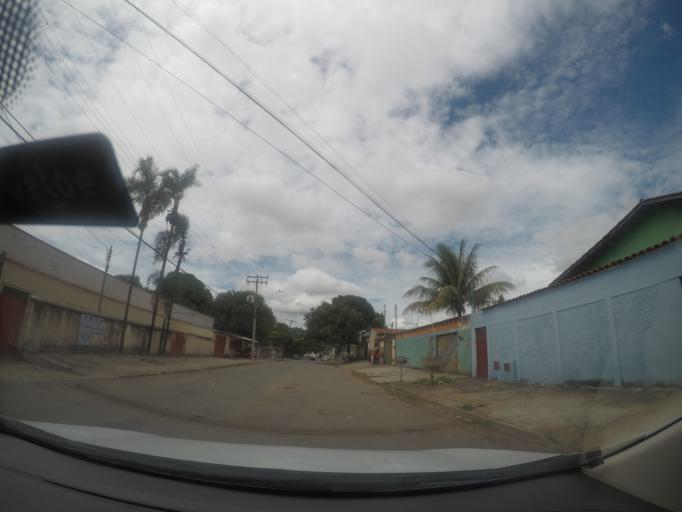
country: BR
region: Goias
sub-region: Goiania
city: Goiania
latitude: -16.6597
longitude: -49.2974
